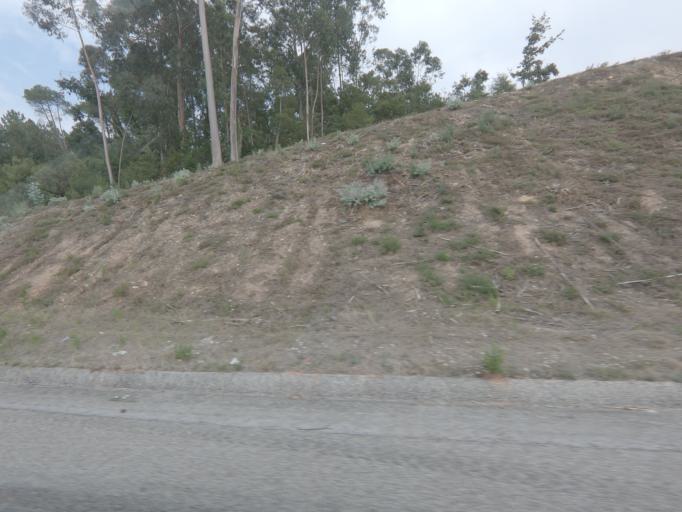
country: PT
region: Coimbra
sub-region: Coimbra
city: Coimbra
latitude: 40.2011
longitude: -8.4536
